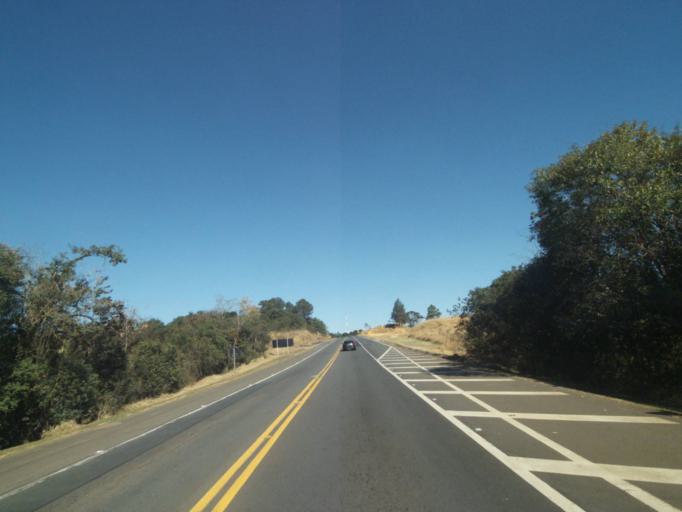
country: BR
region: Parana
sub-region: Tibagi
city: Tibagi
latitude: -24.7401
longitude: -50.5375
